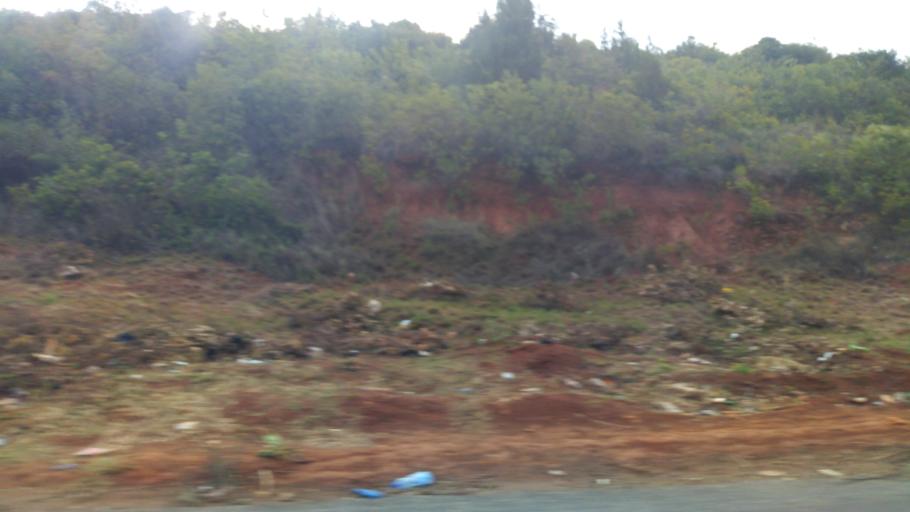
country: KE
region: Kiambu
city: Limuru
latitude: -1.0682
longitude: 36.6013
